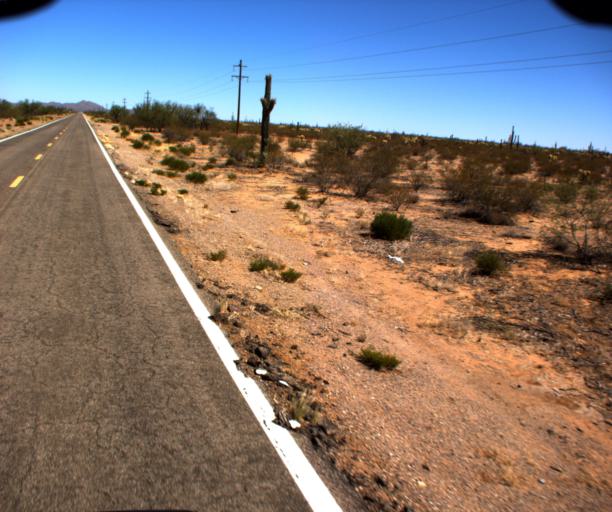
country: US
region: Arizona
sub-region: Pima County
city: Sells
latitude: 32.0937
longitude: -112.0604
